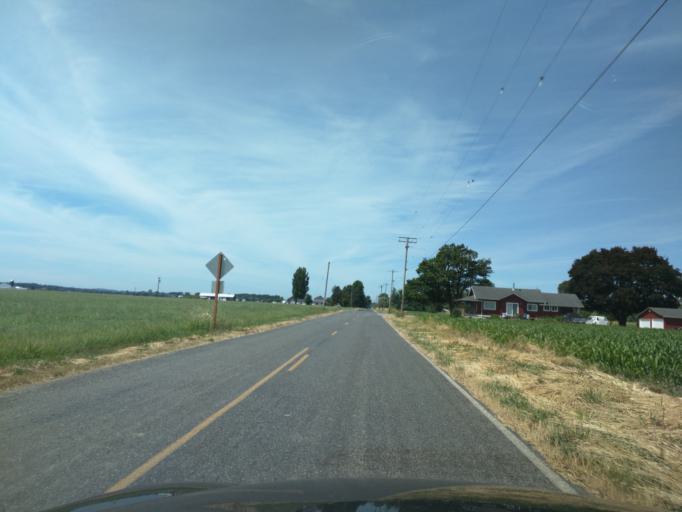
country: US
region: Washington
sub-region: Whatcom County
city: Lynden
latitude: 48.9349
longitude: -122.4212
